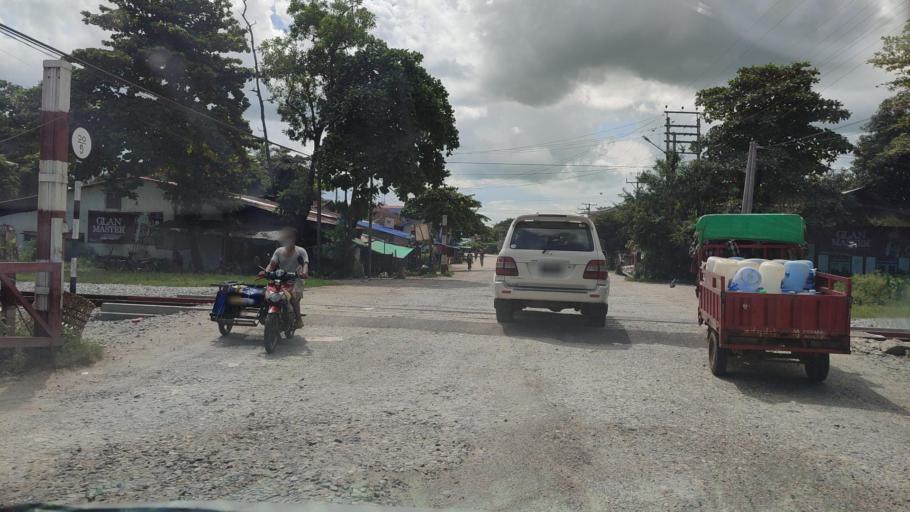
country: MM
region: Bago
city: Nyaunglebin
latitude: 17.9557
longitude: 96.7213
